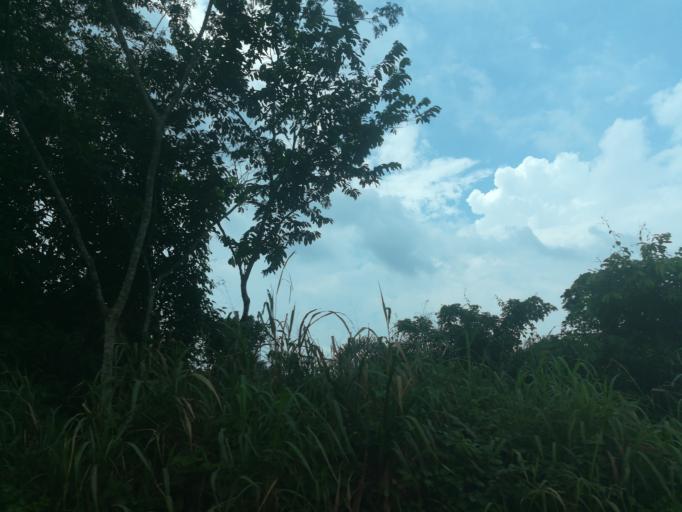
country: NG
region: Lagos
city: Ikorodu
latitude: 6.6683
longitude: 3.6420
